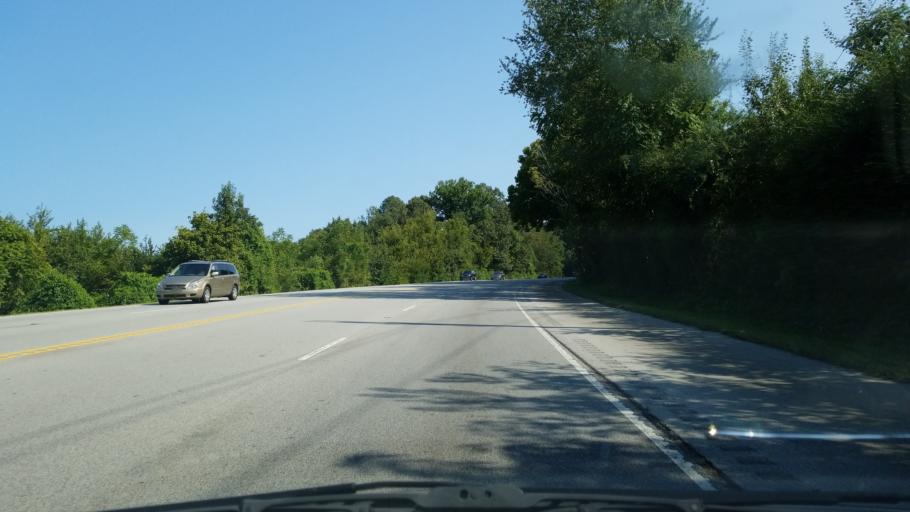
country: US
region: Tennessee
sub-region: Hamilton County
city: East Chattanooga
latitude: 35.0917
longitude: -85.2255
